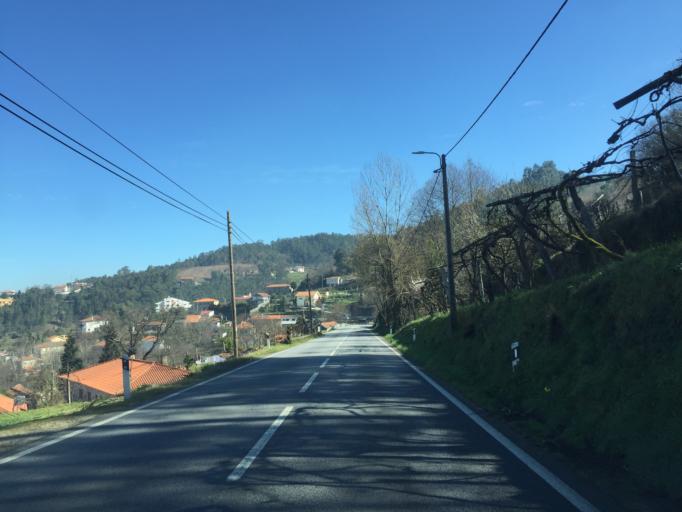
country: PT
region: Aveiro
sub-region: Vale de Cambra
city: Macieira de Cambra
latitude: 40.8936
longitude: -8.3338
